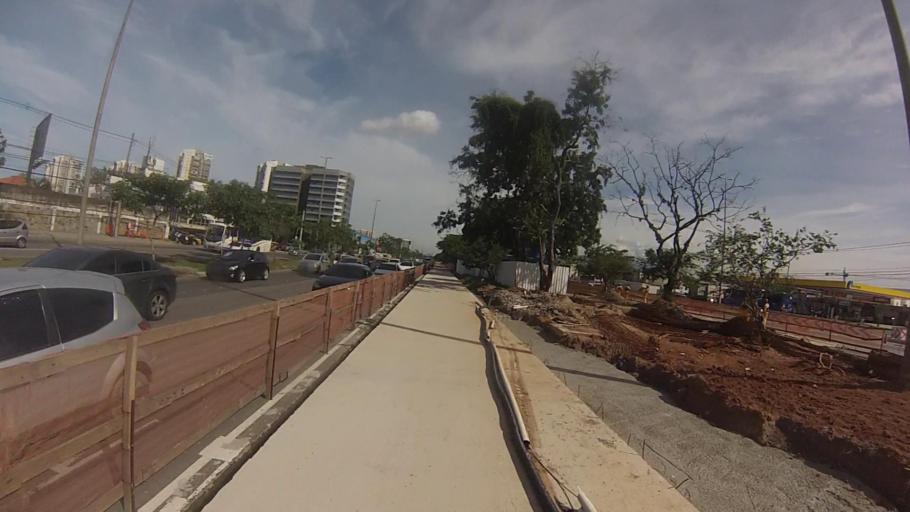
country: BR
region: Rio de Janeiro
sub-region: Rio De Janeiro
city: Rio de Janeiro
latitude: -23.0006
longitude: -43.3361
